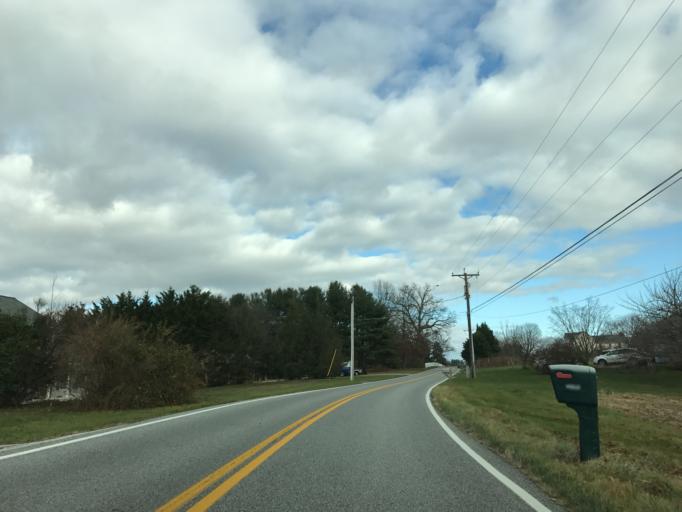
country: US
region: Pennsylvania
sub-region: York County
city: Stewartstown
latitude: 39.6456
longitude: -76.6232
